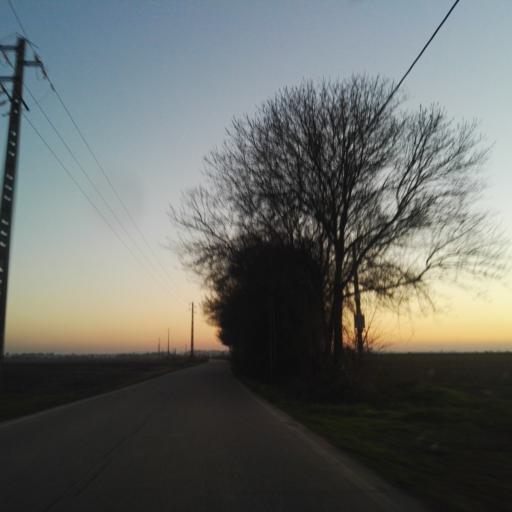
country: PT
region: Santarem
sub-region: Alpiarca
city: Alpiarca
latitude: 39.2778
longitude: -8.5941
